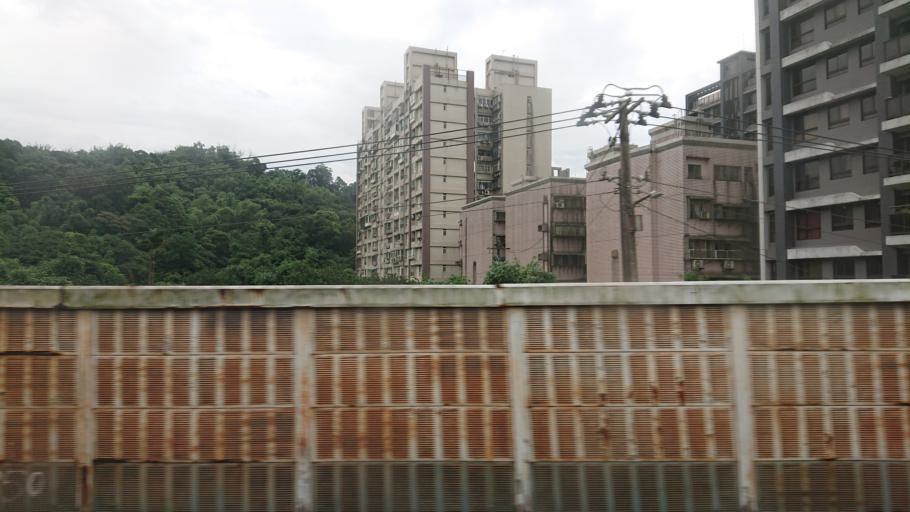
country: TW
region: Taiwan
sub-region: Keelung
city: Keelung
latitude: 25.0822
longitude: 121.6750
